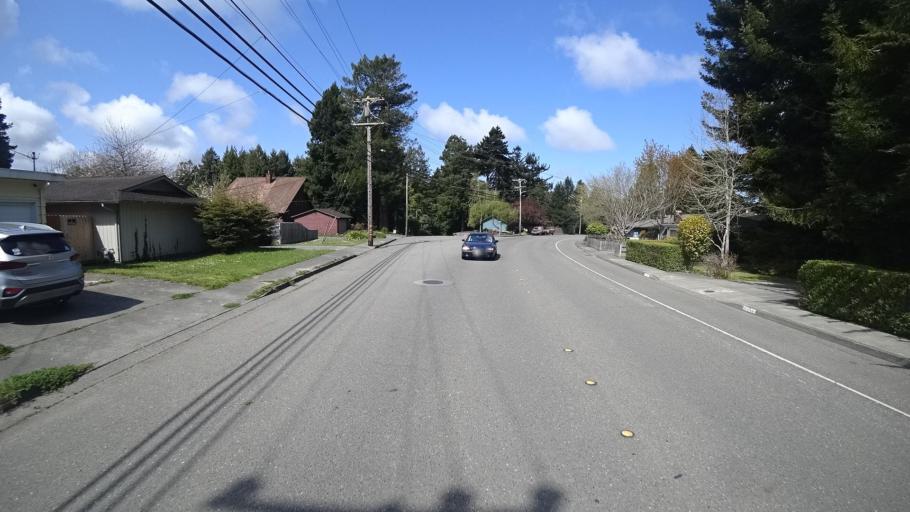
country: US
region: California
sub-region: Humboldt County
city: Cutten
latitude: 40.7588
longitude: -124.1526
